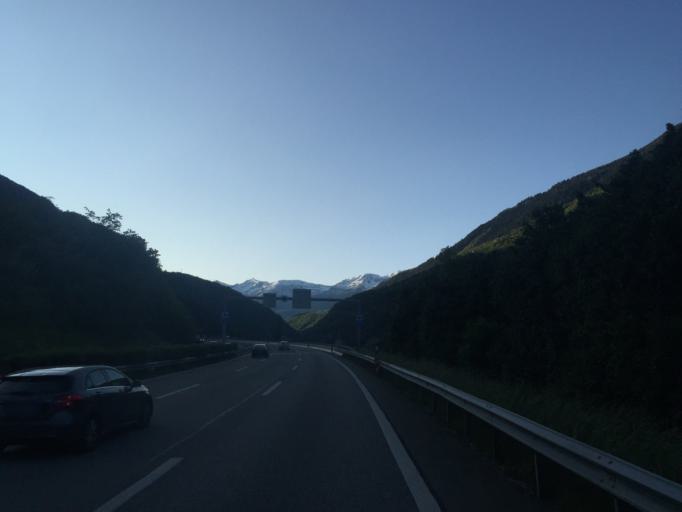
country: CH
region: Ticino
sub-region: Leventina District
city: Bodio
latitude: 46.4095
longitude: 8.8659
